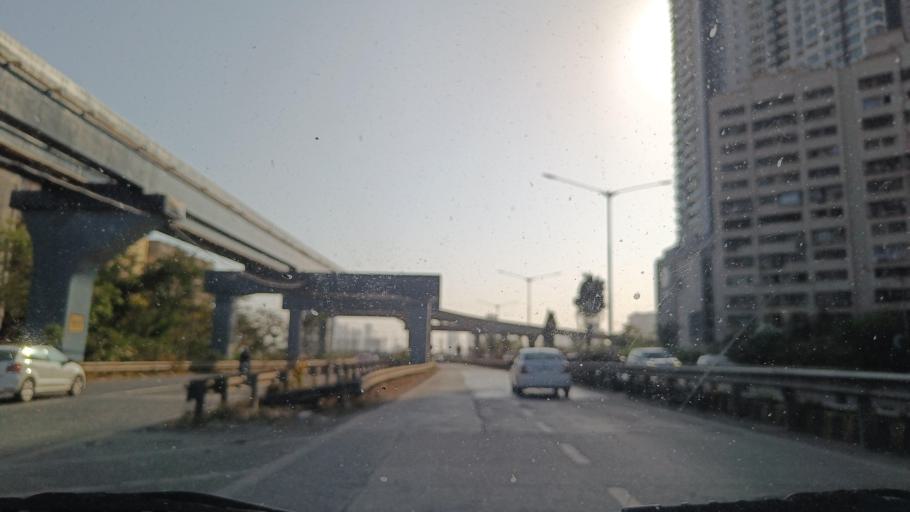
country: IN
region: Maharashtra
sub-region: Mumbai Suburban
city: Mumbai
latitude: 19.0250
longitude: 72.8799
